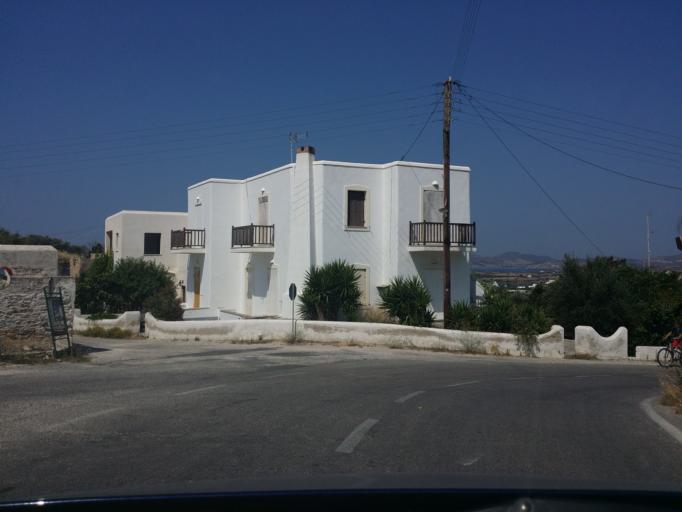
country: GR
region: South Aegean
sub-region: Nomos Kykladon
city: Antiparos
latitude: 37.0022
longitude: 25.1495
